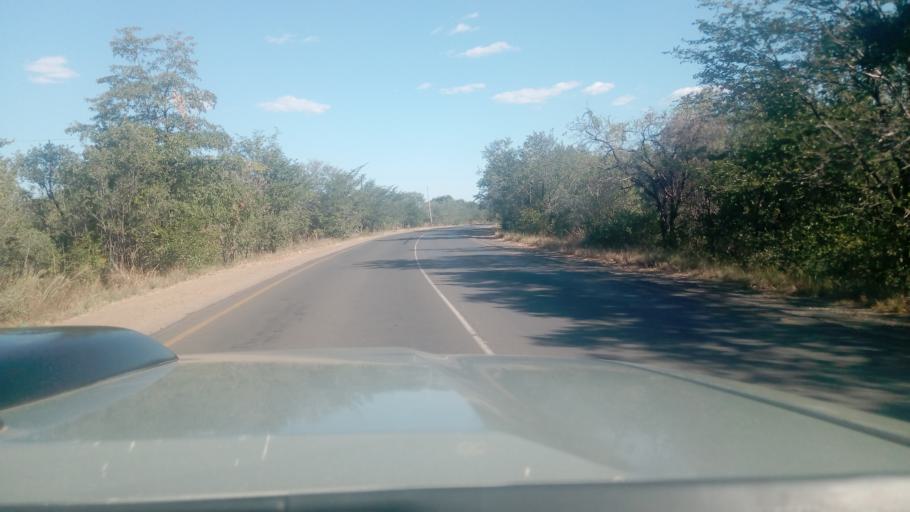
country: ZW
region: Matabeleland North
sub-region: Hwange District
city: Victoria Falls
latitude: -17.9235
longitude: 25.8672
